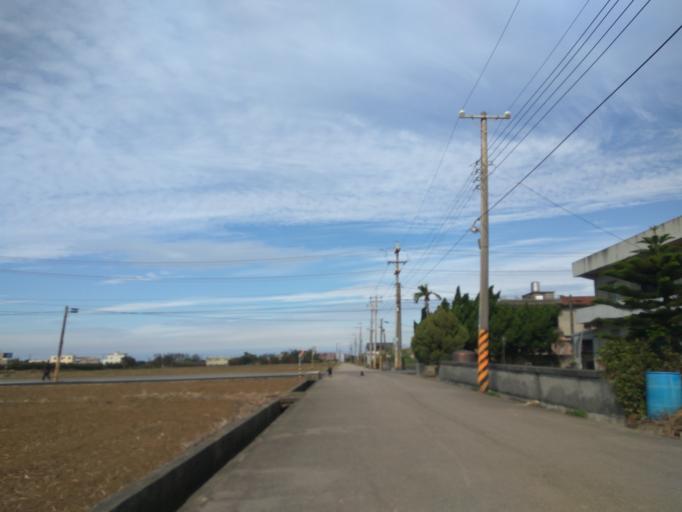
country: TW
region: Taiwan
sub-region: Hsinchu
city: Zhubei
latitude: 24.9870
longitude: 121.0878
